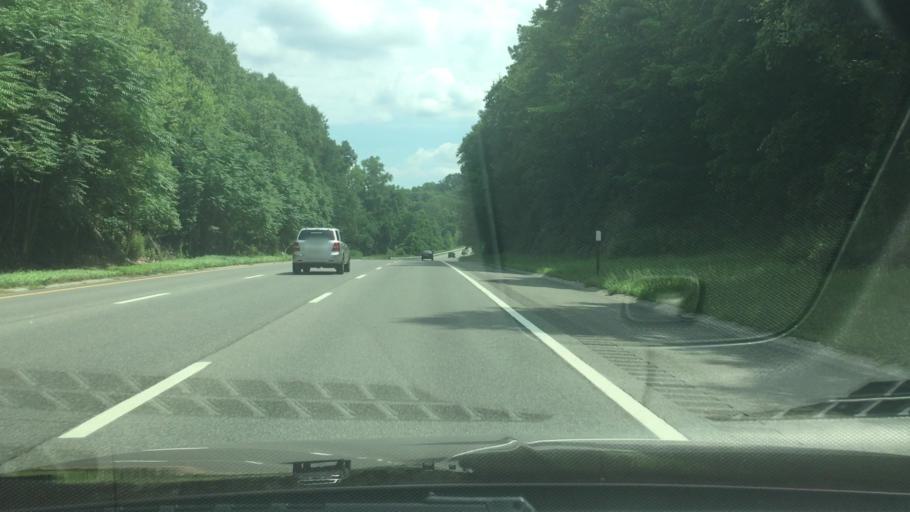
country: US
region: New York
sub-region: Westchester County
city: Yorktown Heights
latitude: 41.2254
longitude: -73.8146
